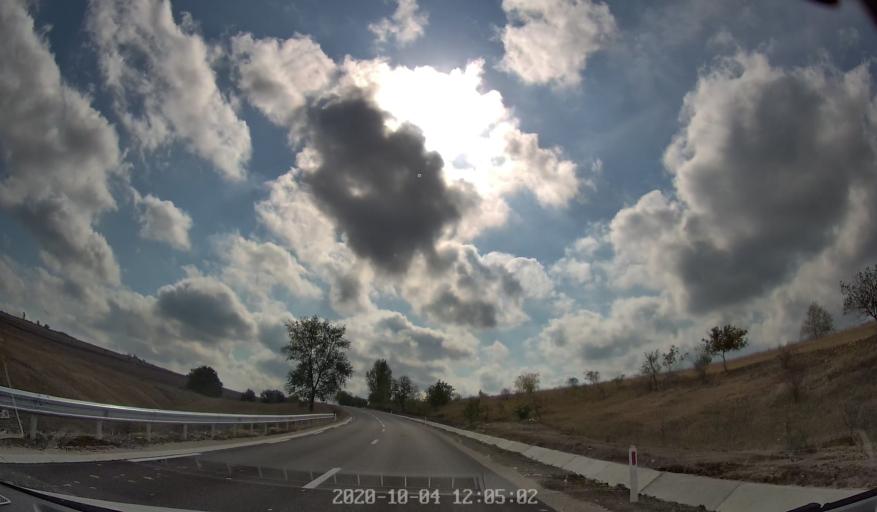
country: MD
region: Rezina
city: Saharna
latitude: 47.5980
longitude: 28.9480
